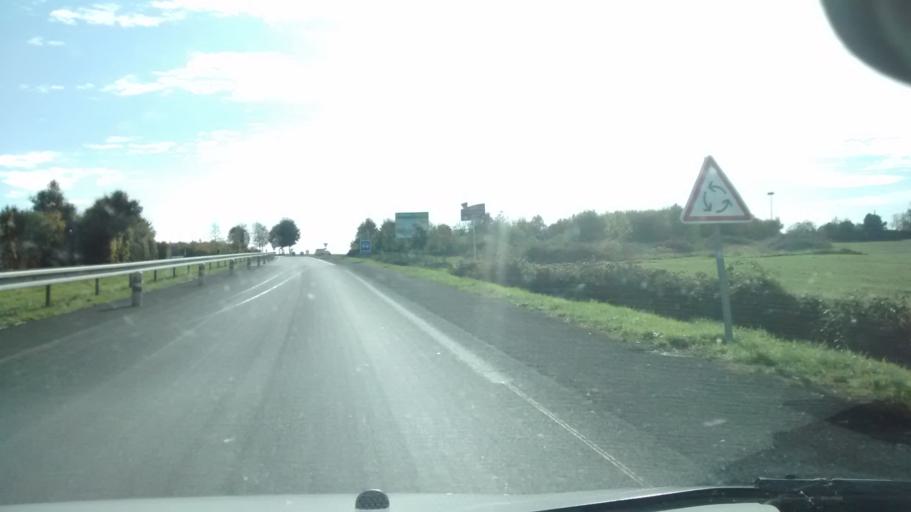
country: FR
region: Pays de la Loire
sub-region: Departement de Maine-et-Loire
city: Pouance
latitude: 47.7496
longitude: -1.1584
